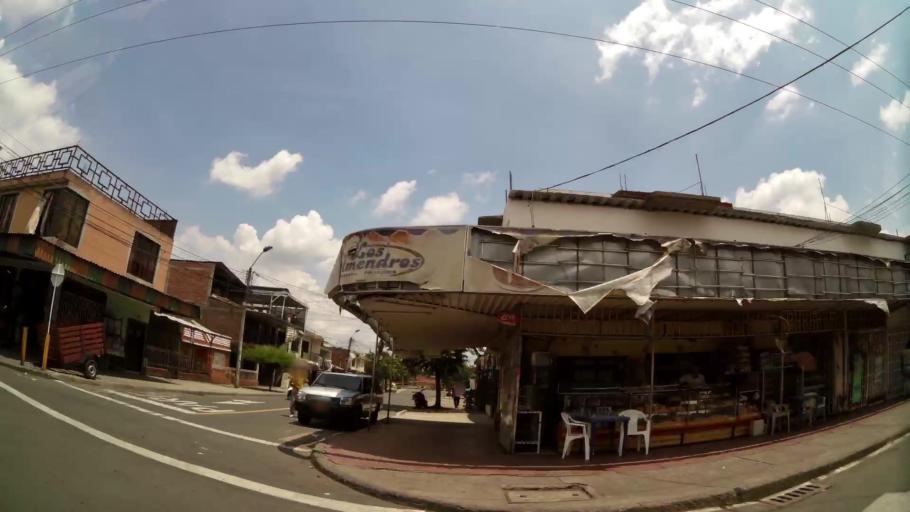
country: CO
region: Valle del Cauca
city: Cali
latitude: 3.4617
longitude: -76.4813
